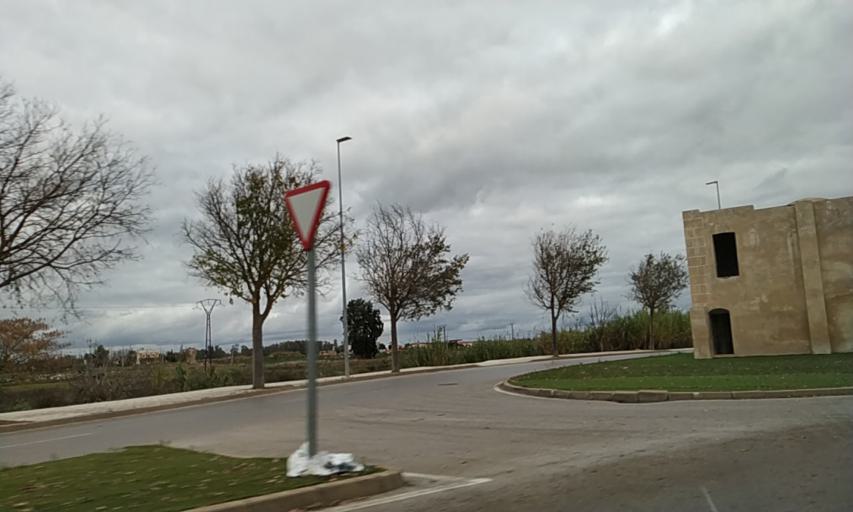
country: ES
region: Extremadura
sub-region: Provincia de Badajoz
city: Badajoz
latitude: 38.8826
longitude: -6.9534
